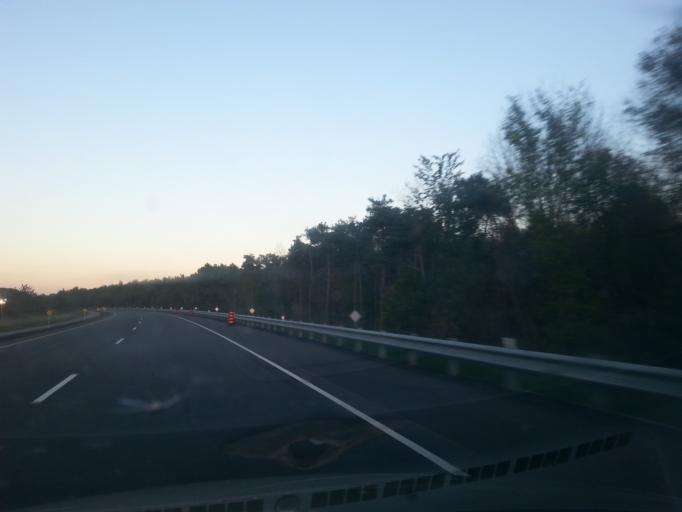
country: CA
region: Ontario
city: Barrie
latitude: 44.5702
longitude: -79.7169
